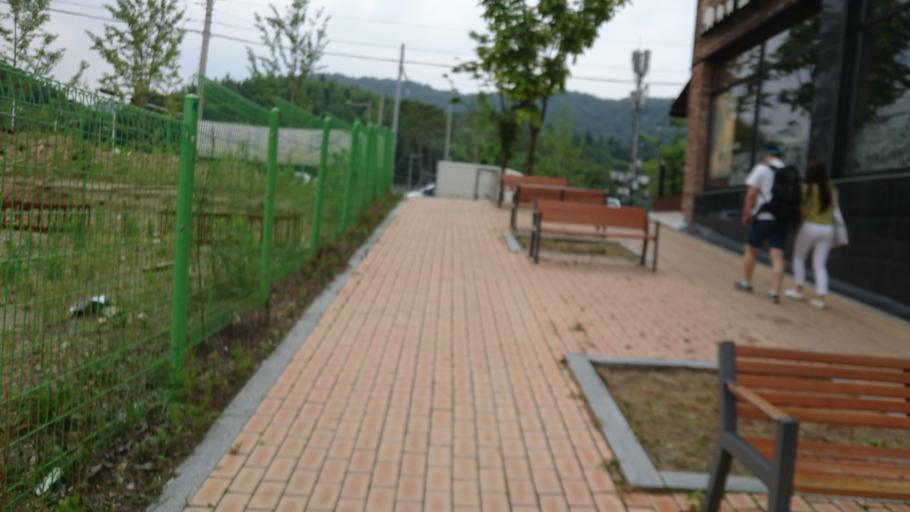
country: KR
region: Daegu
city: Hwawon
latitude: 35.8044
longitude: 128.5198
